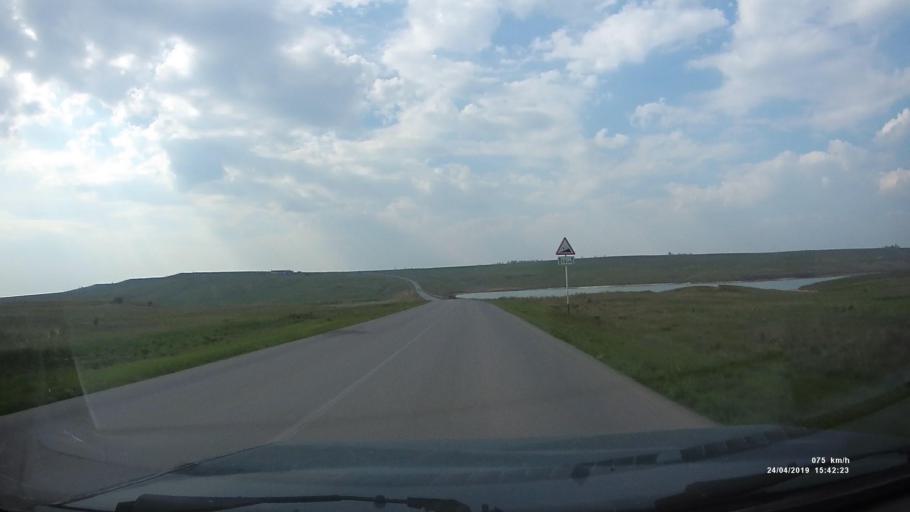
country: RU
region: Kalmykiya
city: Yashalta
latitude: 46.5756
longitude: 42.7886
